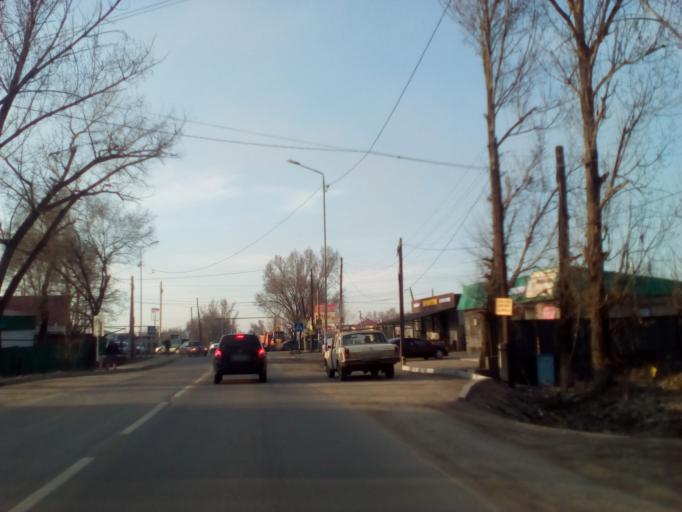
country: KZ
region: Almaty Oblysy
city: Burunday
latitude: 43.2590
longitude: 76.7795
